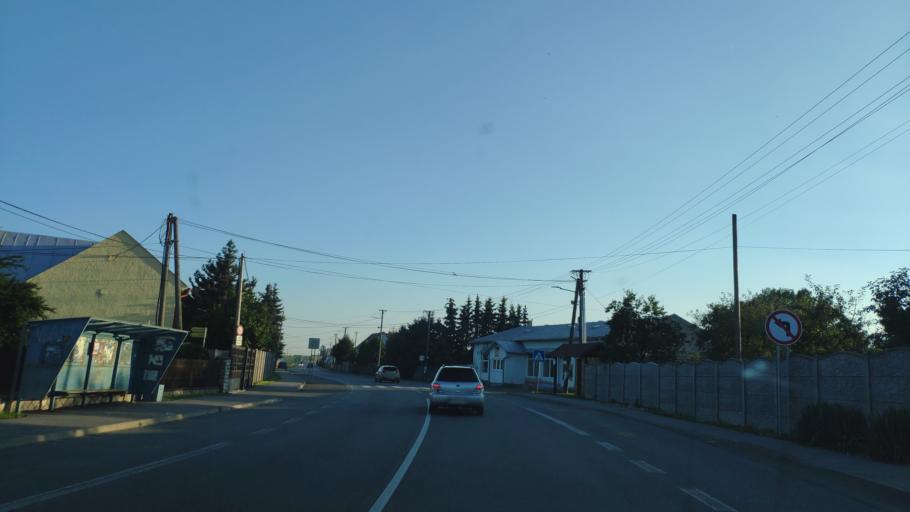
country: SK
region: Presovsky
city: Vranov nad Topl'ou
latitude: 48.8205
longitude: 21.6884
